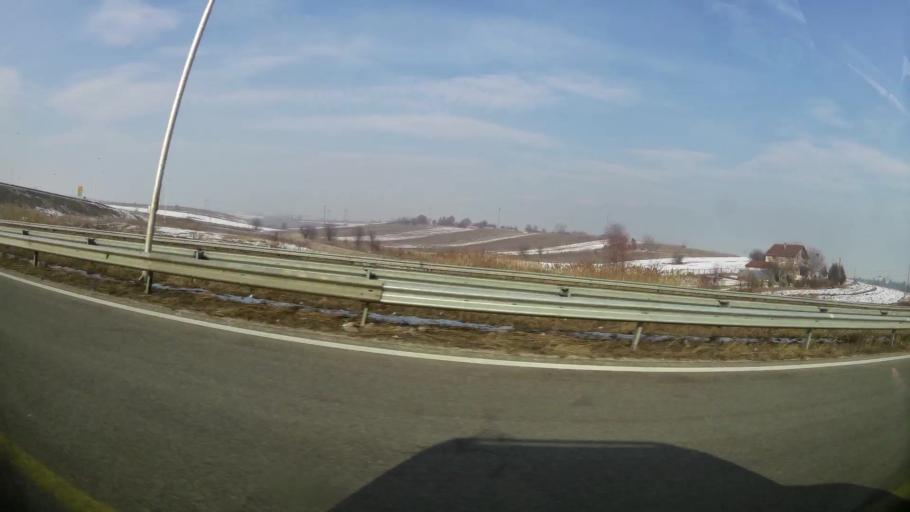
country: MK
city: Creshevo
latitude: 42.0324
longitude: 21.4870
